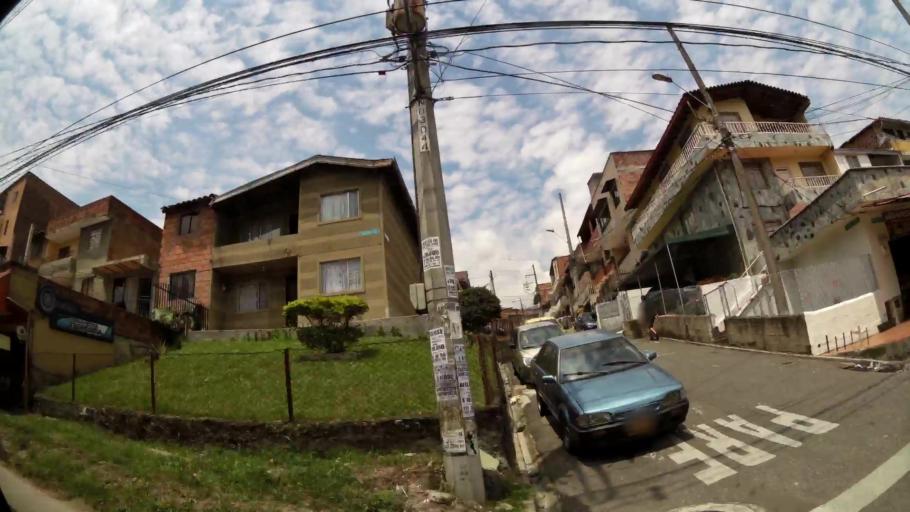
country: CO
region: Antioquia
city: Bello
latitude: 6.3068
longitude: -75.5707
